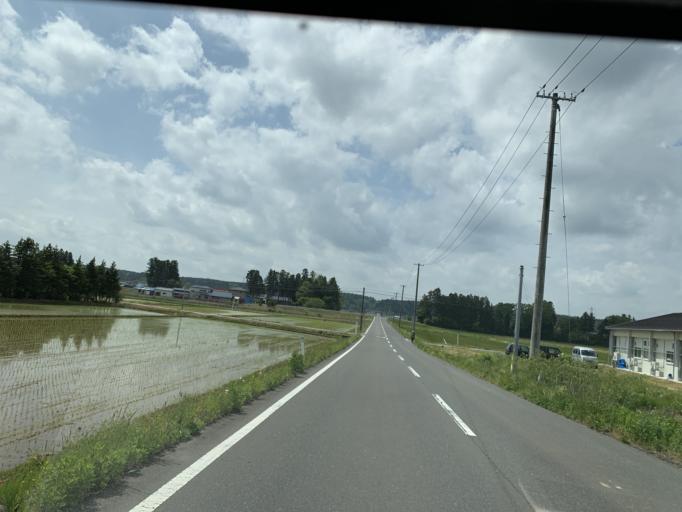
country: JP
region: Miyagi
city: Furukawa
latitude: 38.7519
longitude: 140.9365
